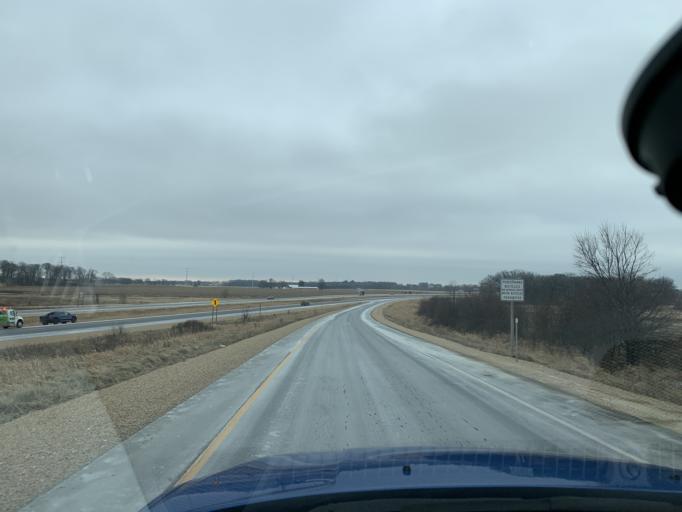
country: US
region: Wisconsin
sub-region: Columbia County
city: Columbus
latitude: 43.3158
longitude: -89.0464
